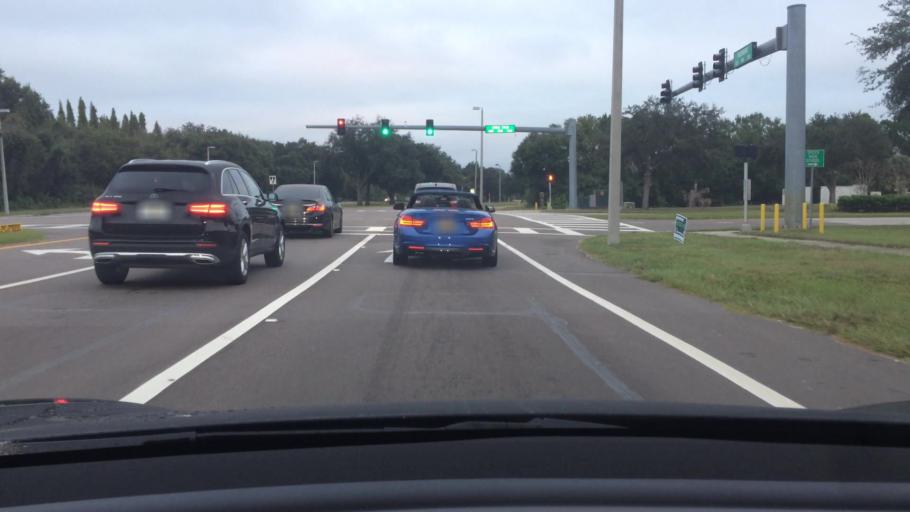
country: US
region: Florida
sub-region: Hillsborough County
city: Progress Village
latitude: 27.8828
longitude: -82.3574
